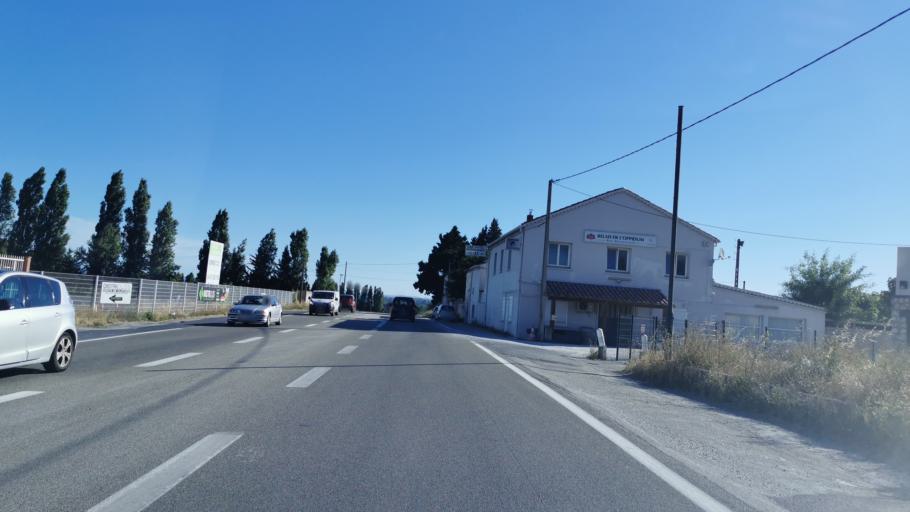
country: FR
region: Languedoc-Roussillon
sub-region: Departement de l'Herault
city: Beziers
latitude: 43.3178
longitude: 3.1846
